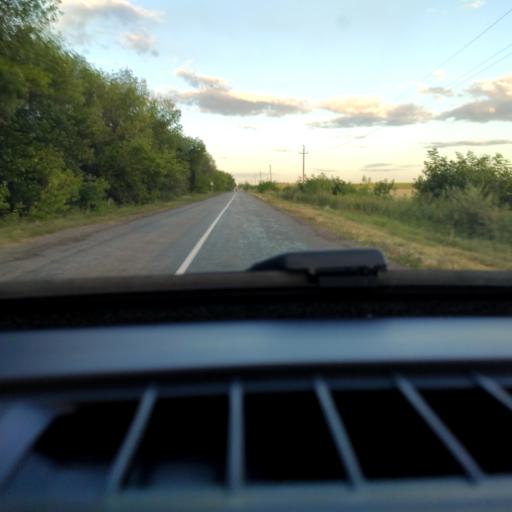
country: RU
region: Voronezj
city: Orlovo
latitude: 51.6449
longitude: 39.7337
